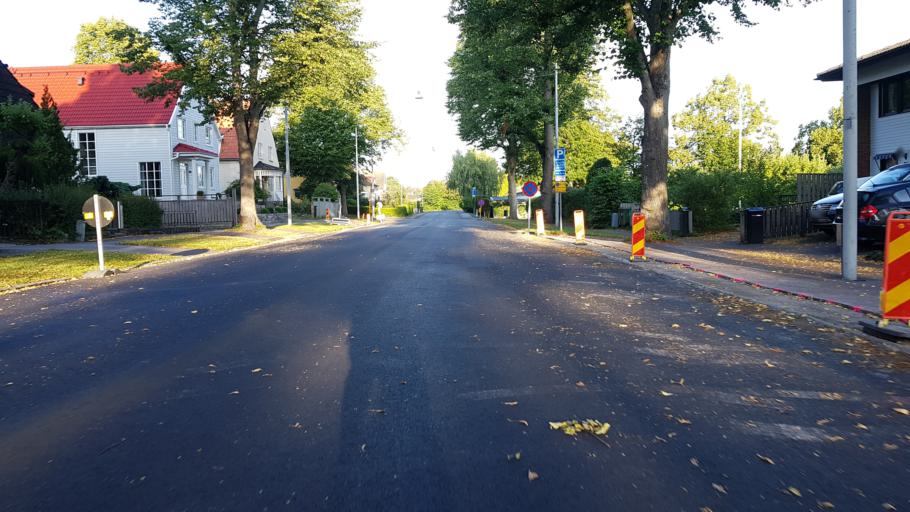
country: SE
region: OEstergoetland
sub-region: Norrkopings Kommun
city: Norrkoping
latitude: 58.5859
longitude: 16.1542
